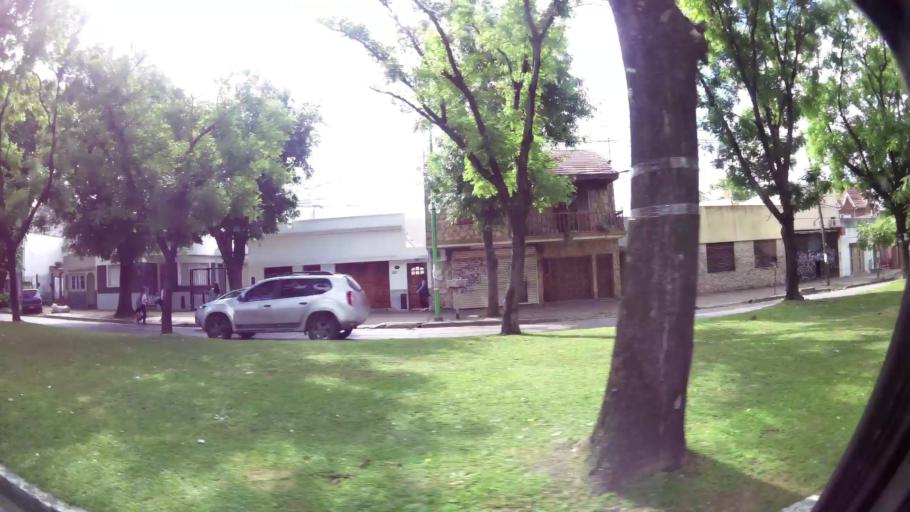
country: AR
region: Buenos Aires
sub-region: Partido de La Plata
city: La Plata
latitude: -34.9163
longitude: -57.9241
